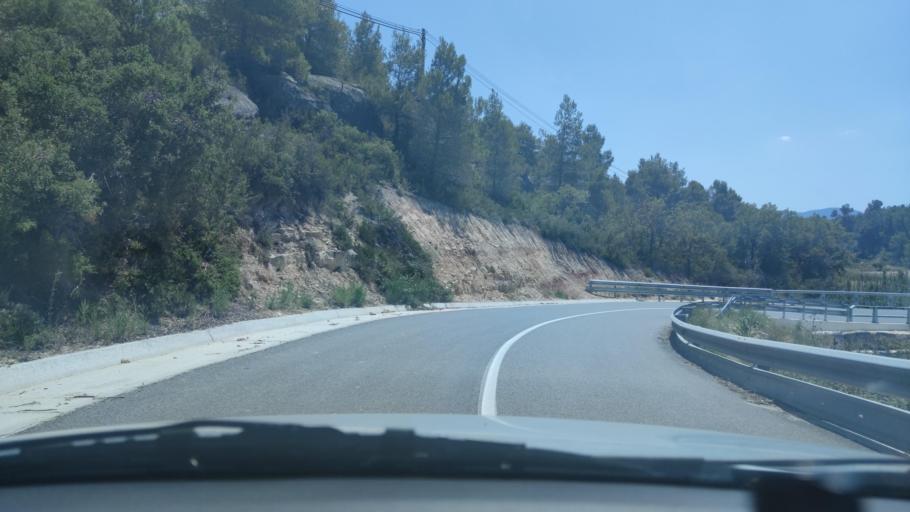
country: ES
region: Catalonia
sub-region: Provincia de Lleida
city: Vinaixa
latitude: 41.4135
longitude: 0.9565
